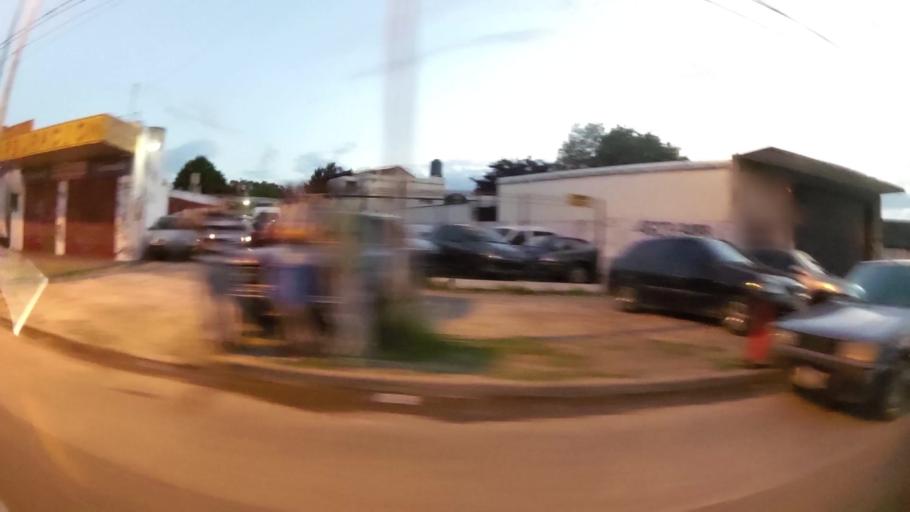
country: AR
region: Buenos Aires
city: Ituzaingo
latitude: -34.6635
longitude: -58.6806
